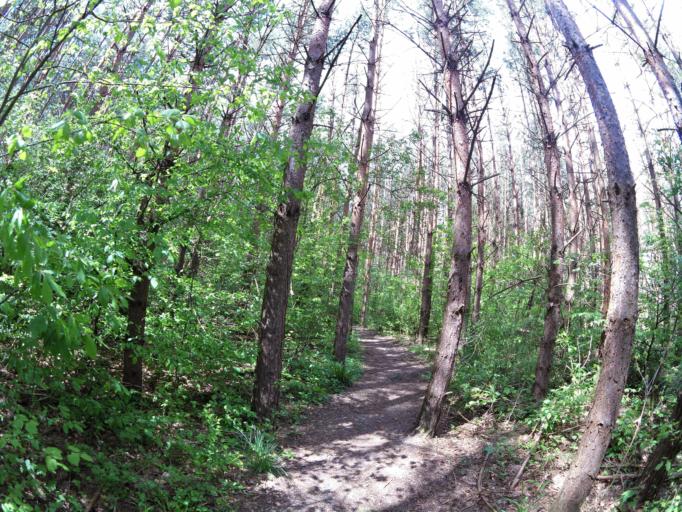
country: DE
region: Thuringia
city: Weberstedt
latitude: 51.0962
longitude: 10.5135
